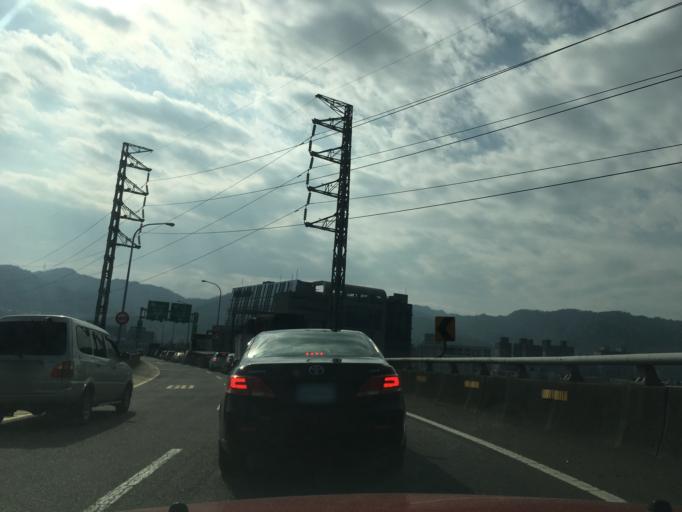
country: TW
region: Taipei
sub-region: Taipei
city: Banqiao
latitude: 24.9724
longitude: 121.4323
